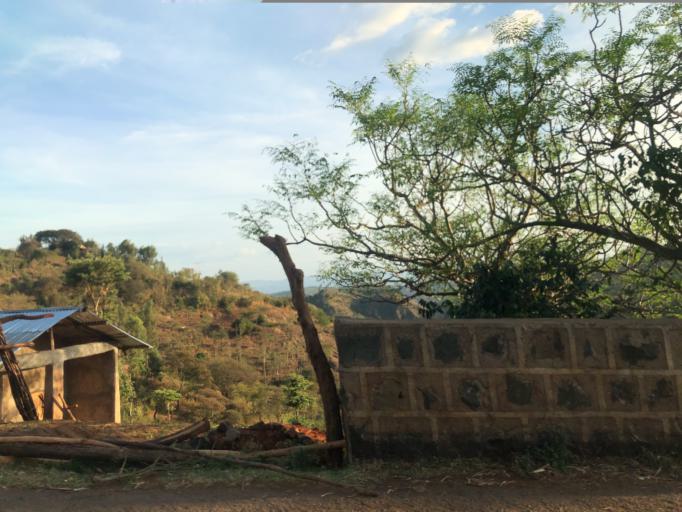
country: ET
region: Southern Nations, Nationalities, and People's Region
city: Konso
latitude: 5.3326
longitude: 37.4139
